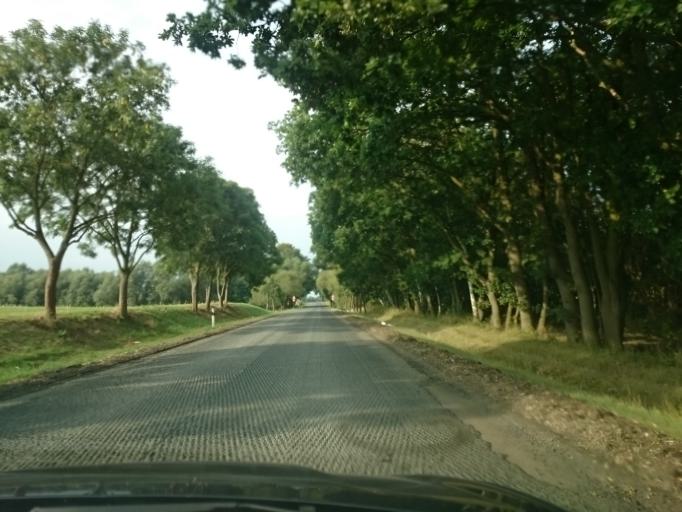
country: DE
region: Mecklenburg-Vorpommern
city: Mollenhagen
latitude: 53.6115
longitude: 12.8871
